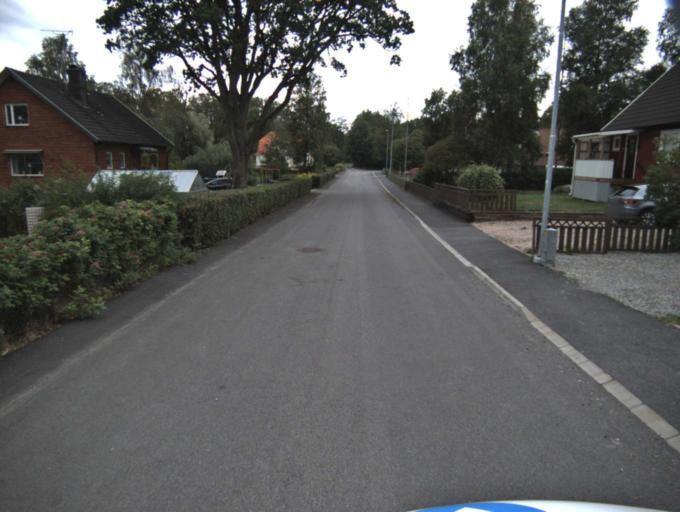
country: SE
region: Vaestra Goetaland
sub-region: Boras Kommun
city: Dalsjofors
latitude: 57.8278
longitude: 13.1905
